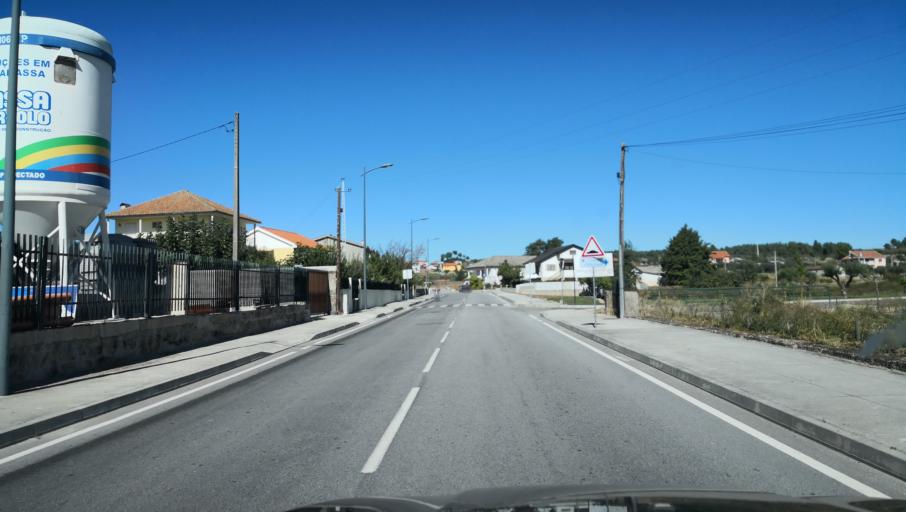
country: PT
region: Vila Real
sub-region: Valpacos
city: Valpacos
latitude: 41.5940
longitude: -7.3062
